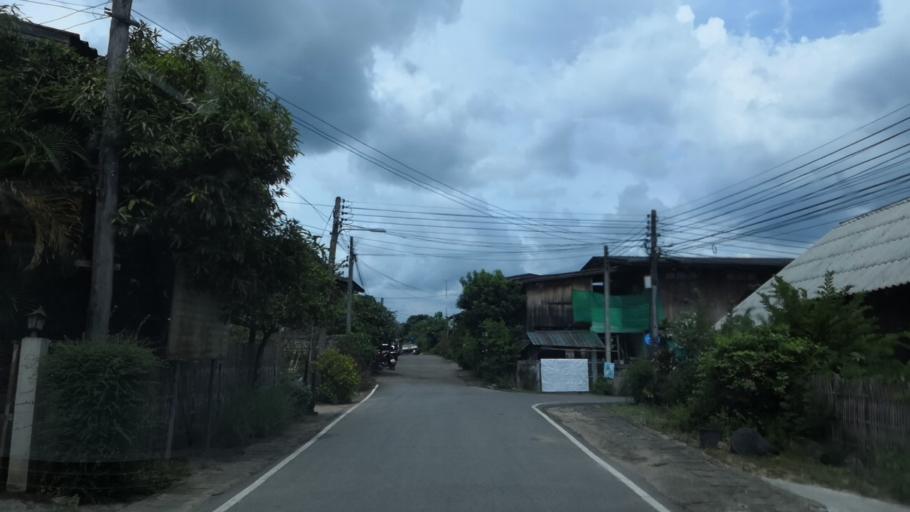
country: TH
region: Mae Hong Son
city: Khun Yuam
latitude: 18.7400
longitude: 97.9251
